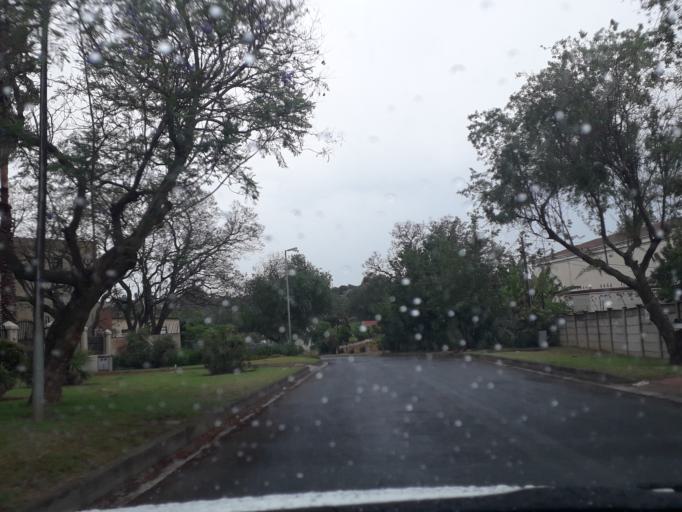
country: ZA
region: Gauteng
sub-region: City of Johannesburg Metropolitan Municipality
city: Roodepoort
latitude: -26.0906
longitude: 27.9392
